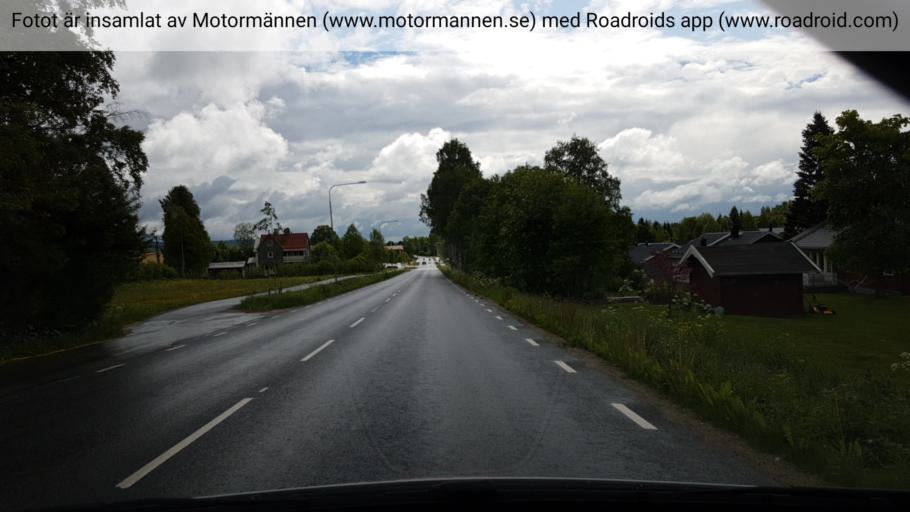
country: SE
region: Vaesterbotten
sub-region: Vannas Kommun
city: Vannasby
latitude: 63.9151
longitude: 19.8076
